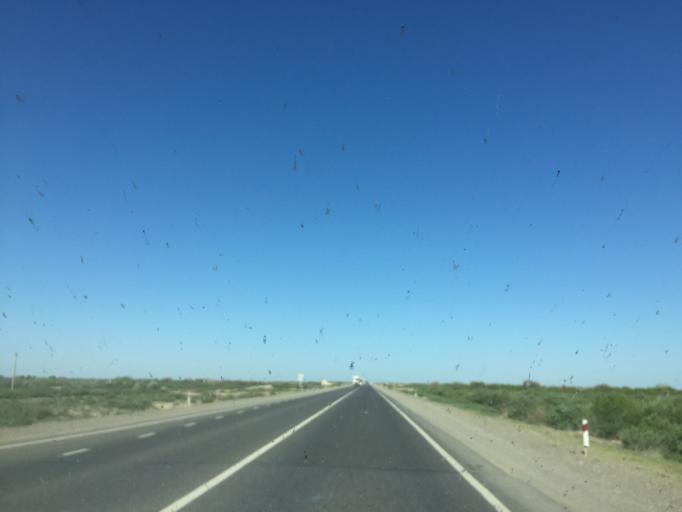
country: KZ
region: Qyzylorda
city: Terenozek
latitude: 44.8630
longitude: 64.8514
